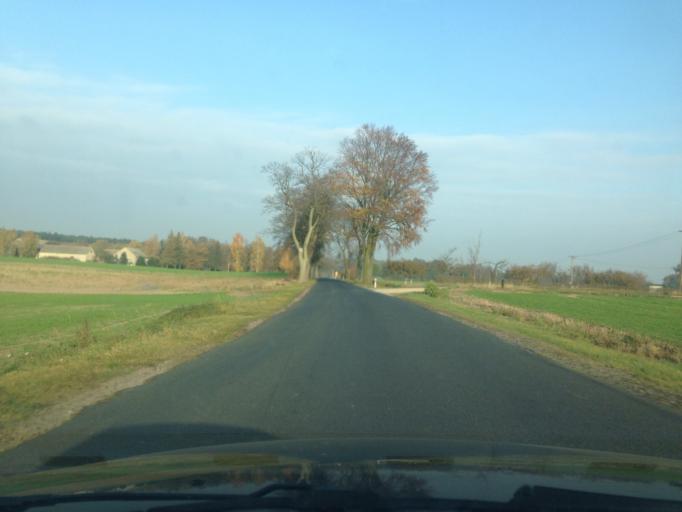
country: PL
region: Kujawsko-Pomorskie
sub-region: Powiat wabrzeski
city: Debowa Laka
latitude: 53.2536
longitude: 19.0498
